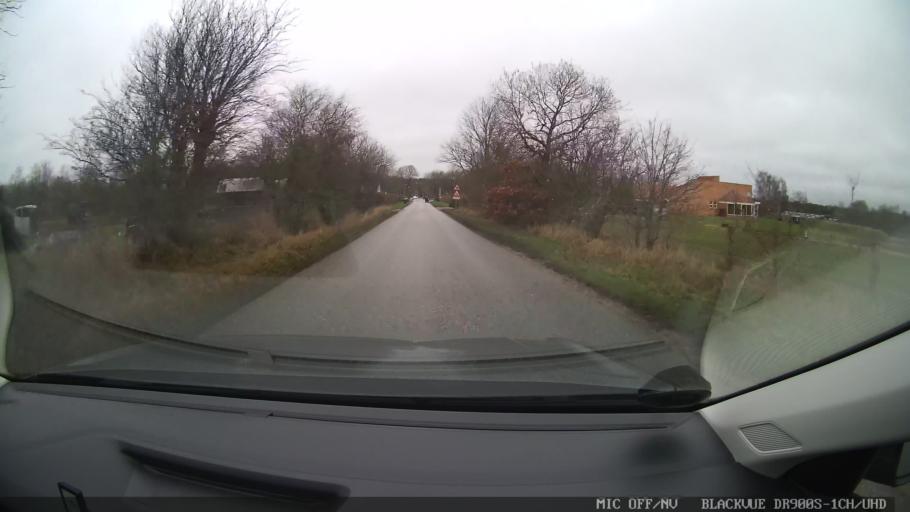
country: DK
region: Central Jutland
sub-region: Viborg Kommune
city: Viborg
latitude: 56.4214
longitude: 9.3815
